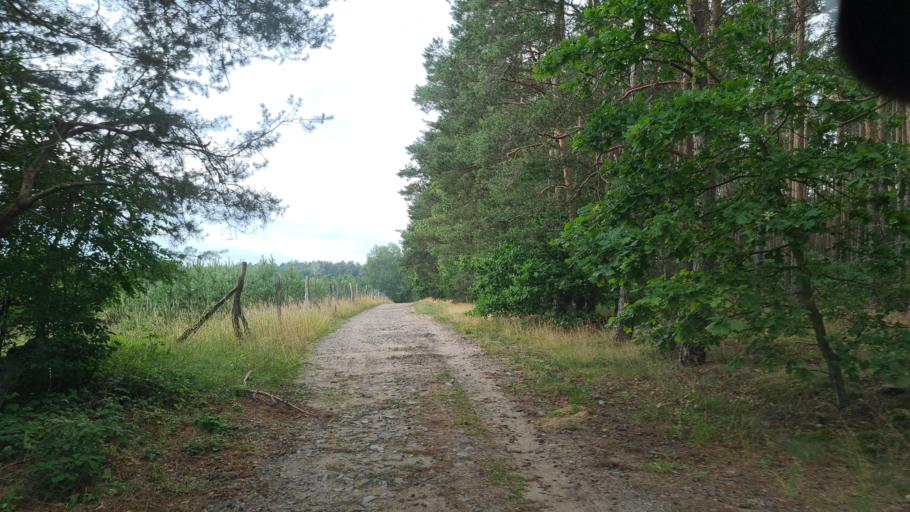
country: DE
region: Brandenburg
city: Sonnewalde
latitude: 51.7282
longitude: 13.6986
